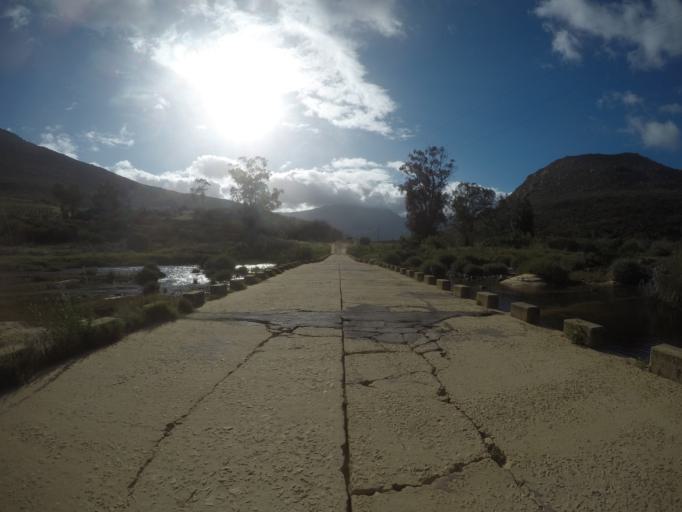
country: ZA
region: Western Cape
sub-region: West Coast District Municipality
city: Clanwilliam
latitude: -32.3657
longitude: 18.9539
